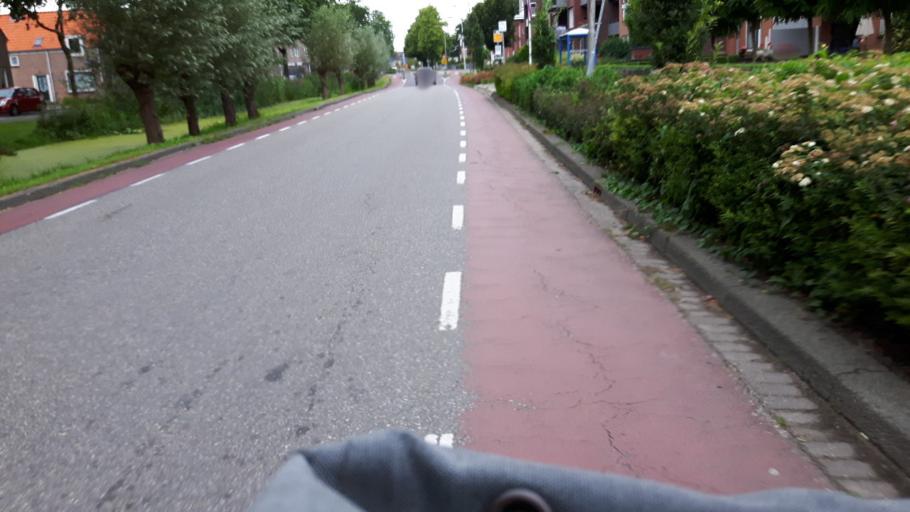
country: NL
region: South Holland
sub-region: Gemeente Vlist
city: Haastrecht
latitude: 51.9984
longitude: 4.7782
